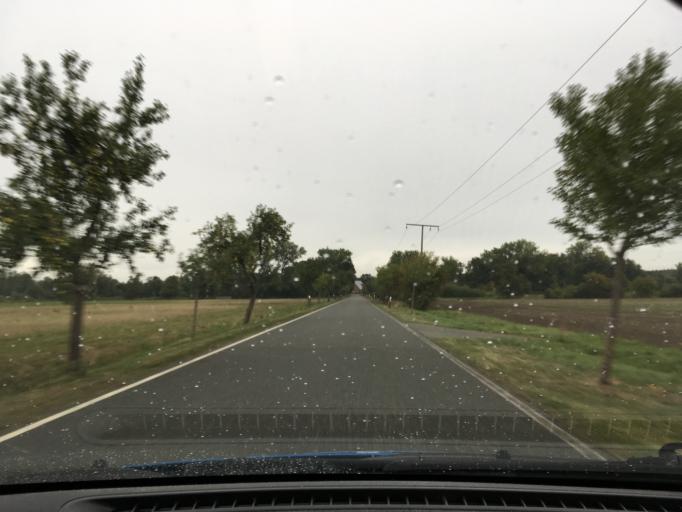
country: DE
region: Lower Saxony
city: Hitzacker
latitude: 53.2214
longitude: 10.9876
